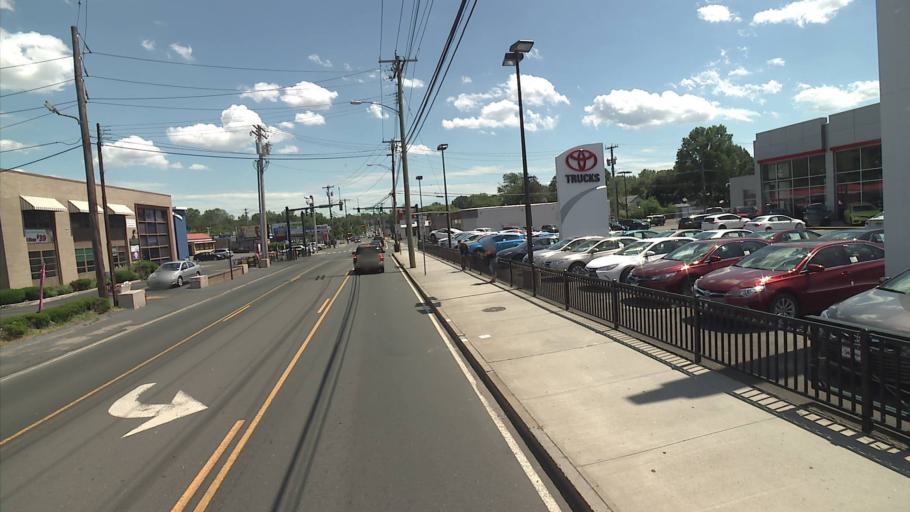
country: US
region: Connecticut
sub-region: New Haven County
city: Woodbridge
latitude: 41.3361
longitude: -72.9782
